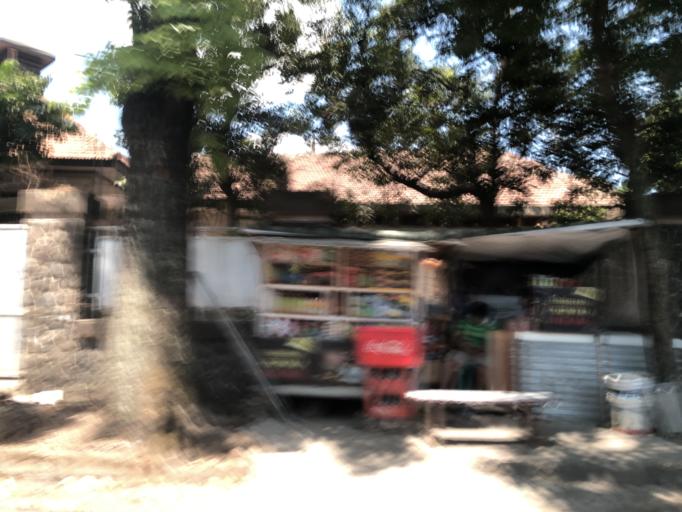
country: ID
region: West Java
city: Bandung
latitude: -6.9122
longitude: 107.6323
